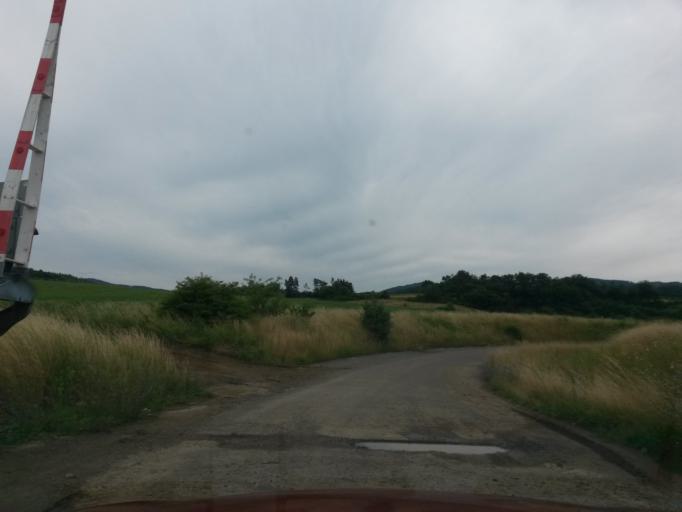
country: SK
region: Banskobystricky
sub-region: Okres Banska Bystrica
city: Zvolen
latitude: 48.5605
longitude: 19.2422
